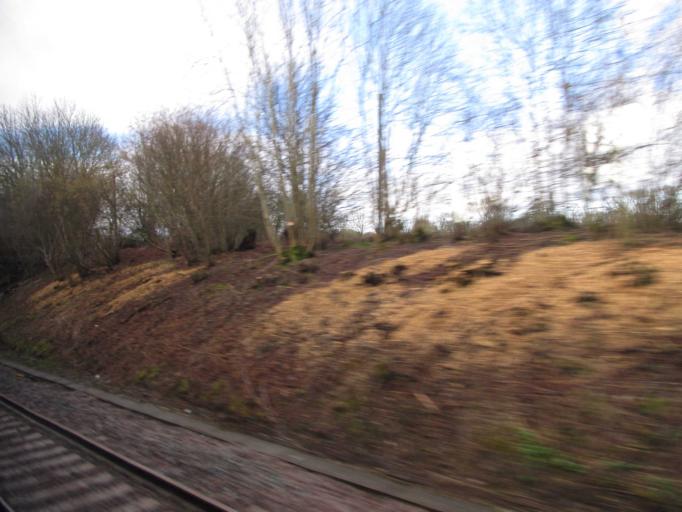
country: GB
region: England
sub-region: Hampshire
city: Old Basing
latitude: 51.3027
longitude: -1.0557
